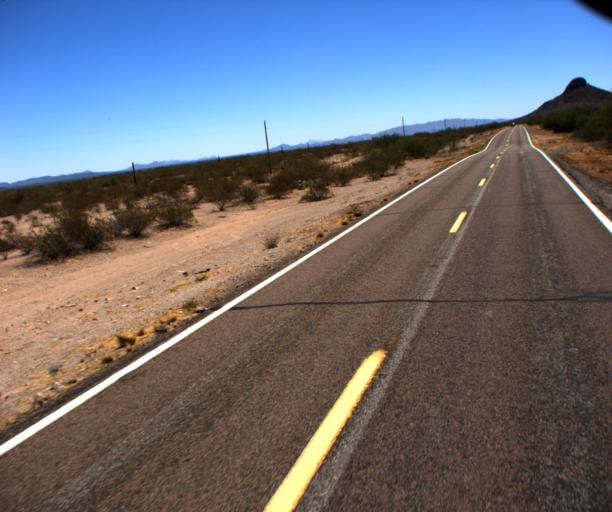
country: US
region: Arizona
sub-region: Pima County
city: Ajo
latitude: 32.2049
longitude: -112.5531
